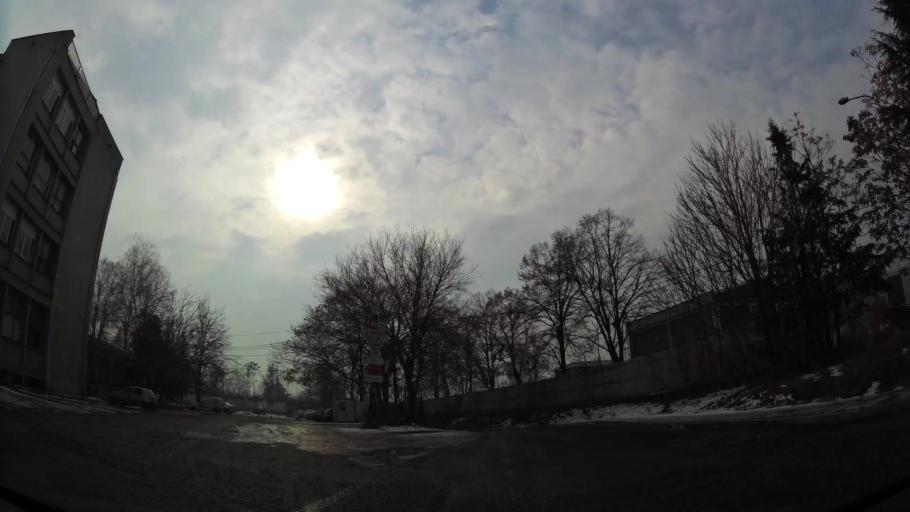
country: MK
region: Cair
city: Cair
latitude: 41.9986
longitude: 21.4691
